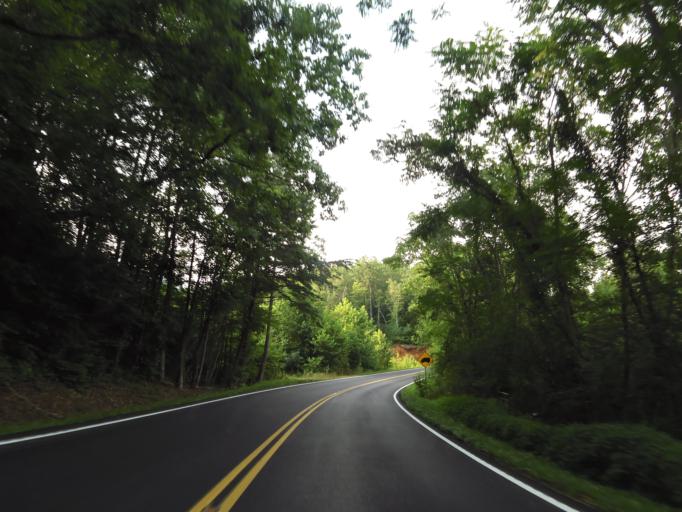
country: US
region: Tennessee
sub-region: Morgan County
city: Coalfield
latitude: 36.0770
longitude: -84.4589
